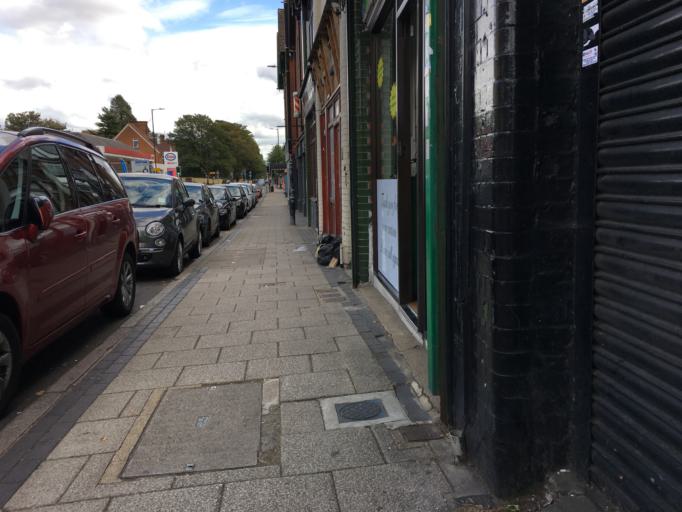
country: GB
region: England
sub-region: Hertfordshire
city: St Albans
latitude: 51.7485
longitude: -0.3331
